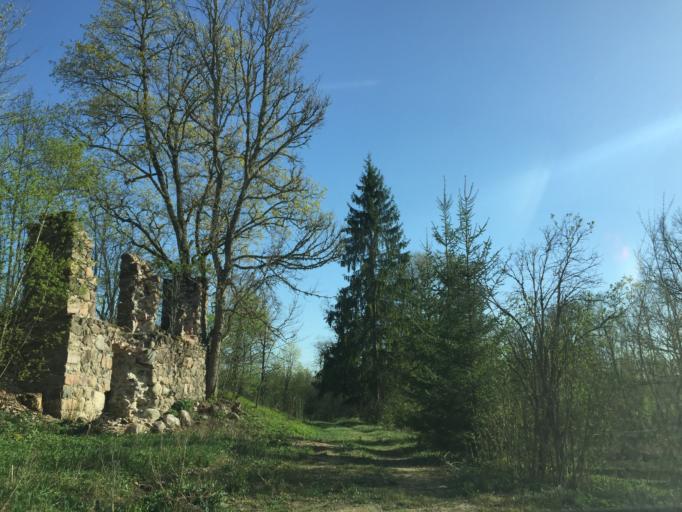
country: LV
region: Ergli
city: Ergli
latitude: 56.8689
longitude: 25.4757
